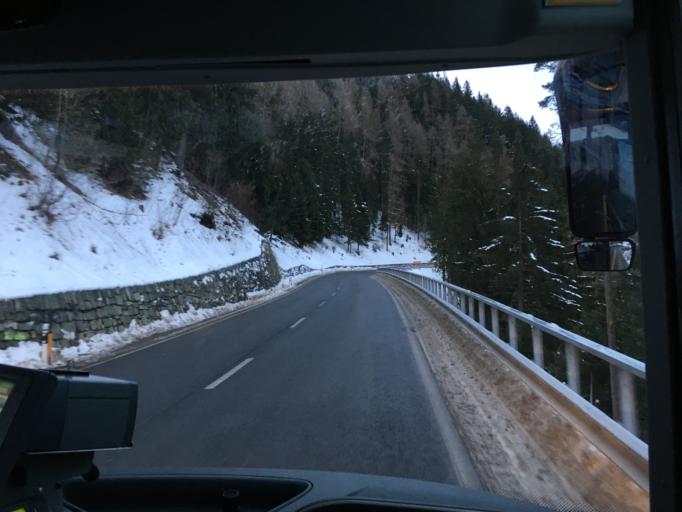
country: CH
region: Grisons
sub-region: Albula District
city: Tiefencastel
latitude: 46.5724
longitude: 9.6234
